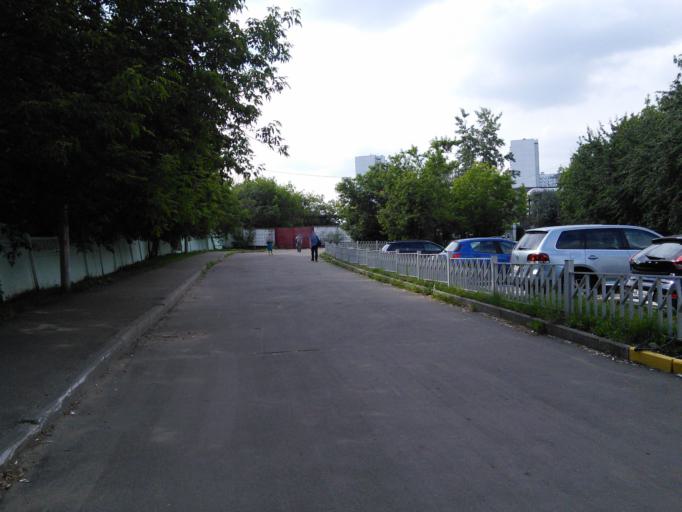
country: RU
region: Moskovskaya
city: Cheremushki
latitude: 55.6600
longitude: 37.5371
